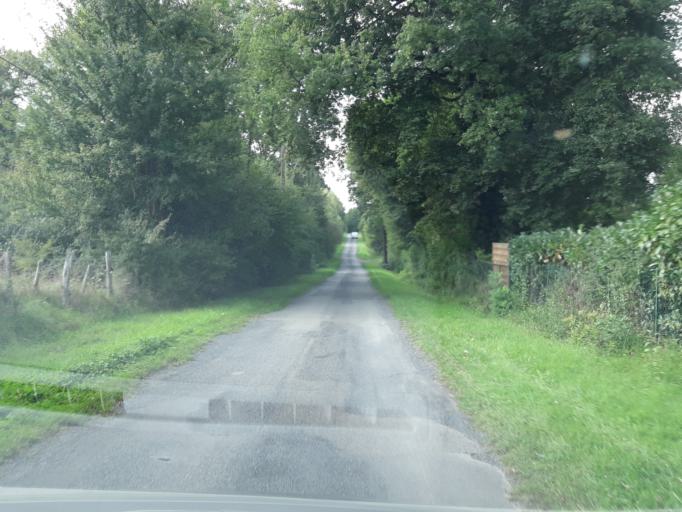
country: FR
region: Centre
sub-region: Departement du Loiret
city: Chilleurs-aux-Bois
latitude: 48.0499
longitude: 2.1631
